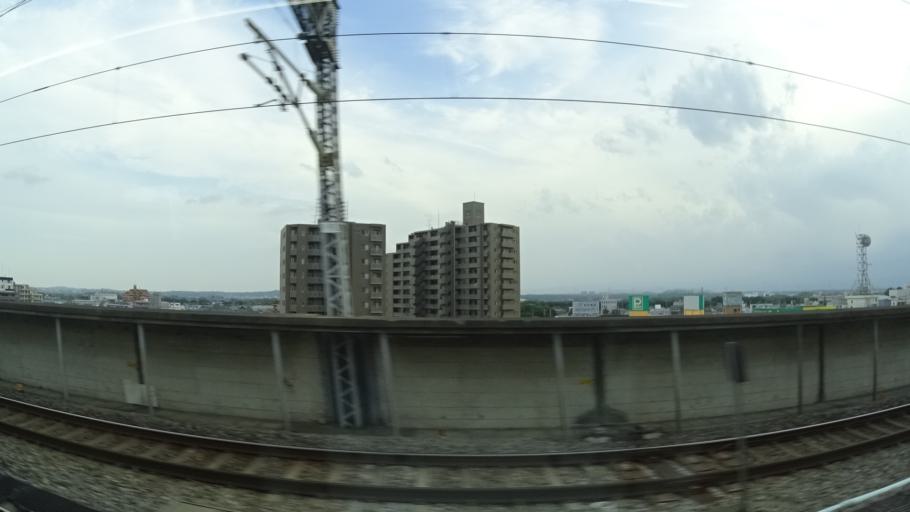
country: JP
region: Saitama
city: Kumagaya
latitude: 36.1388
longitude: 139.3914
